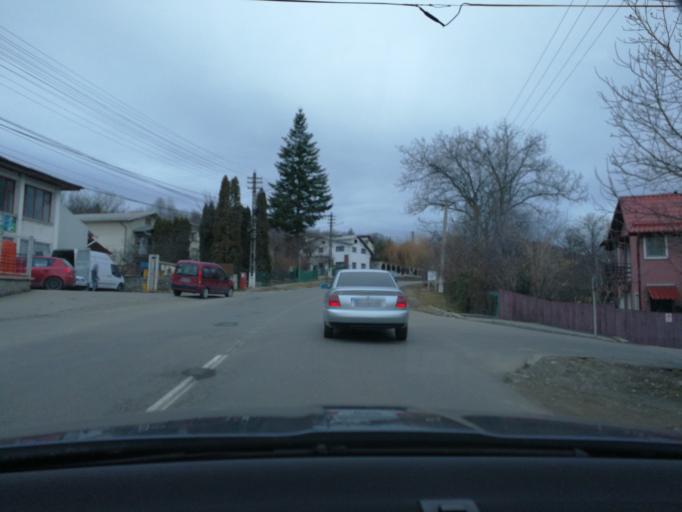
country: RO
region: Prahova
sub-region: Comuna Cornu
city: Cornu de Jos
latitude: 45.1496
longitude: 25.6894
